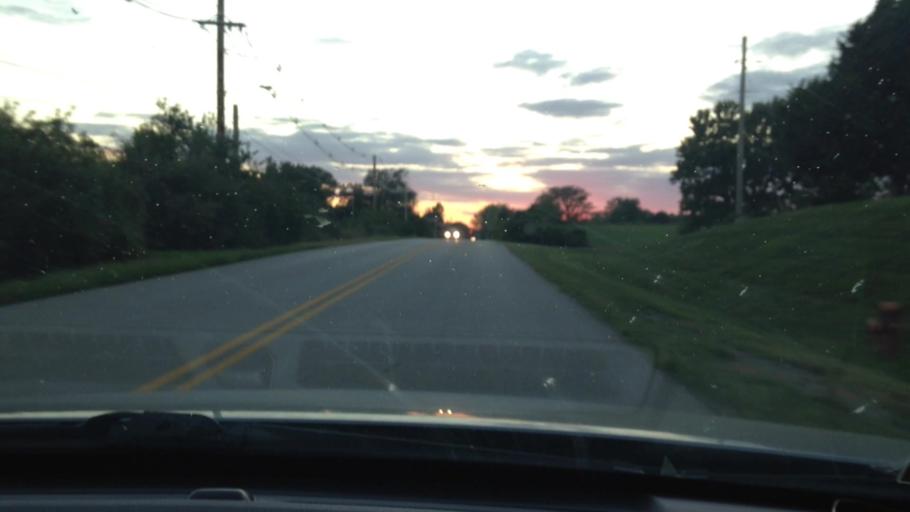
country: US
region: Kansas
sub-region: Leavenworth County
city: Lansing
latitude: 39.1868
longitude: -94.8580
